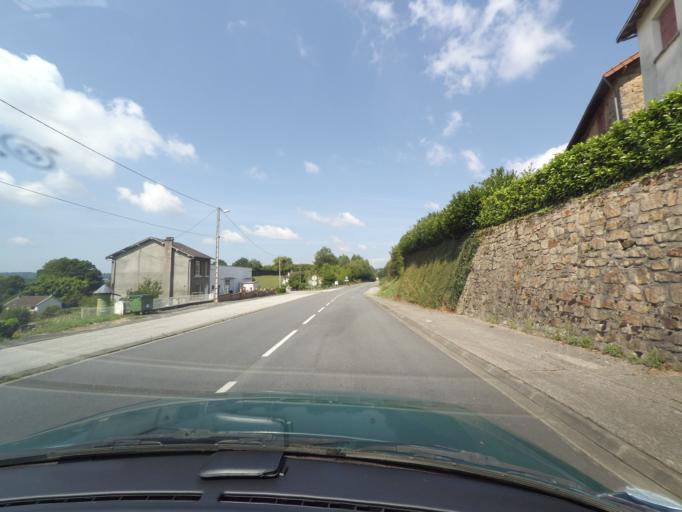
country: FR
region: Limousin
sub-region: Departement de la Haute-Vienne
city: Neuvic-Entier
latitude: 45.7635
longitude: 1.5673
